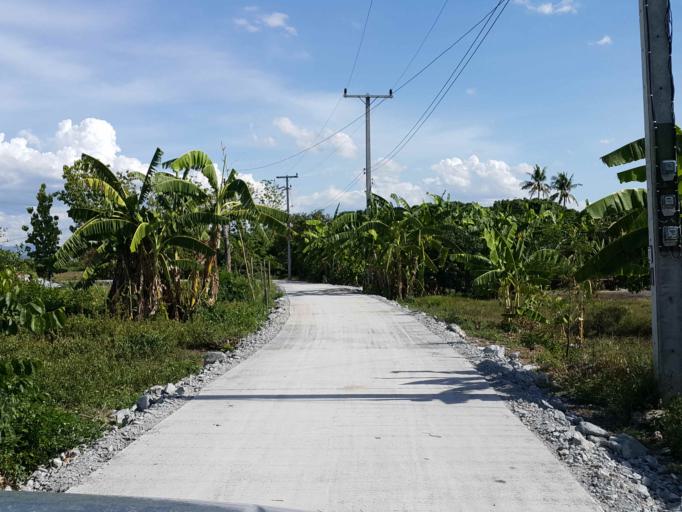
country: TH
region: Chiang Mai
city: San Kamphaeng
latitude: 18.8006
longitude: 99.1482
